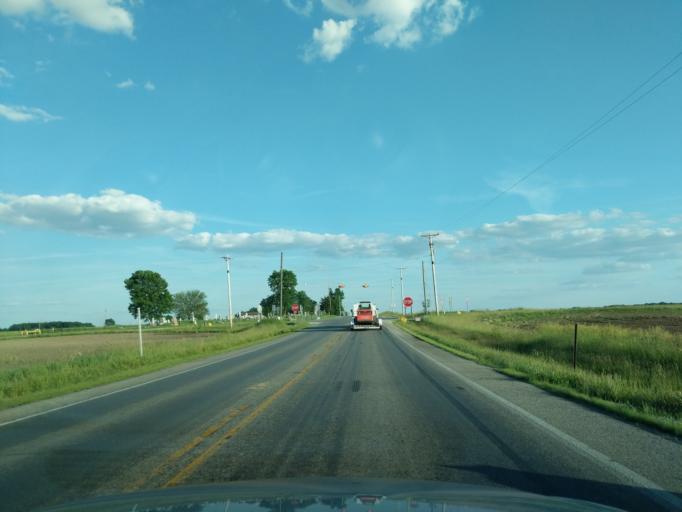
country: US
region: Indiana
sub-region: Huntington County
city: Warren
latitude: 40.7427
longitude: -85.4448
